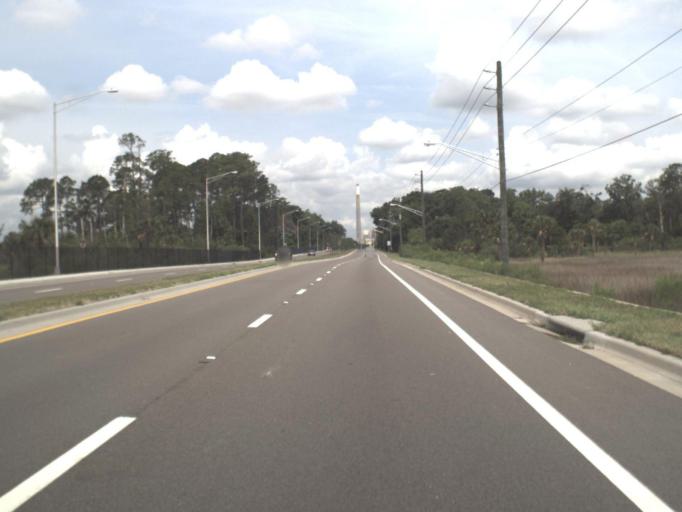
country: US
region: Florida
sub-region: Duval County
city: Jacksonville
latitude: 30.4141
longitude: -81.5897
